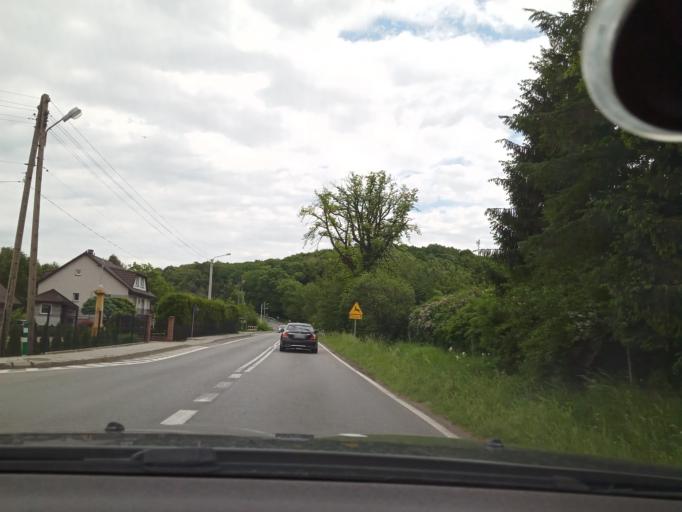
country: PL
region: Lesser Poland Voivodeship
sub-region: Powiat wielicki
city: Tomaszkowice
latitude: 49.9737
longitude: 20.1101
